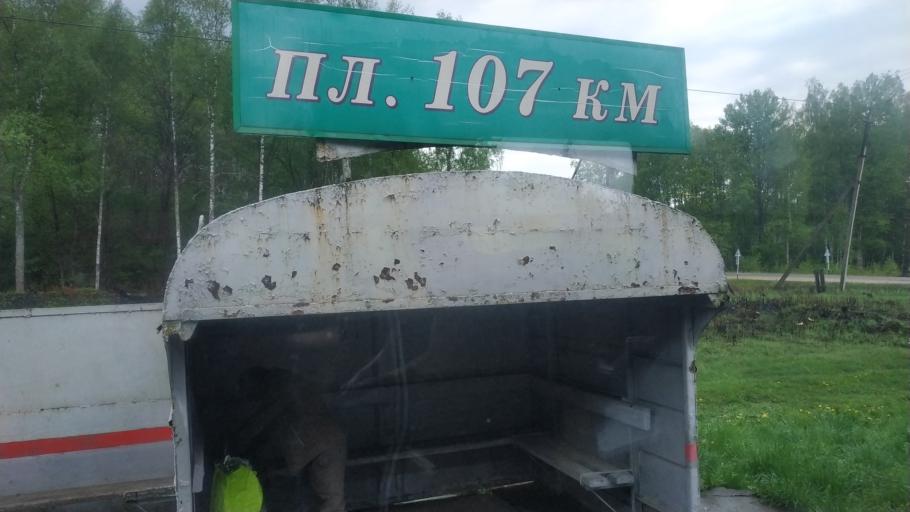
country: RU
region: Kaluga
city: Baryatino
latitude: 54.2920
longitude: 34.3400
